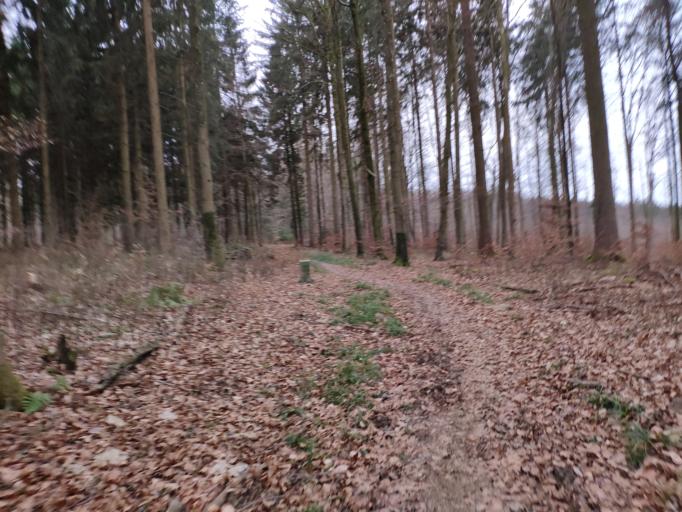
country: DE
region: Baden-Wuerttemberg
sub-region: Freiburg Region
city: Inzlingen
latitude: 47.6004
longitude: 7.6926
